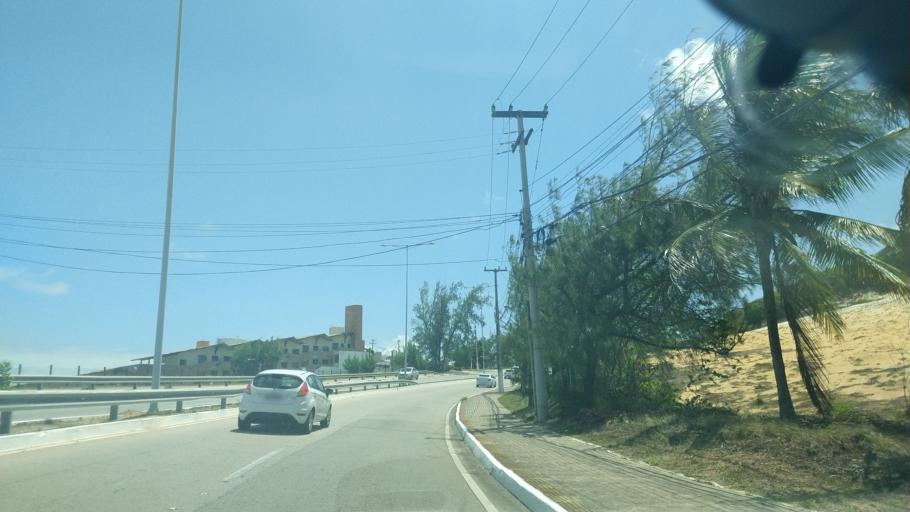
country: BR
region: Rio Grande do Norte
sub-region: Natal
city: Natal
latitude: -5.8645
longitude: -35.1808
